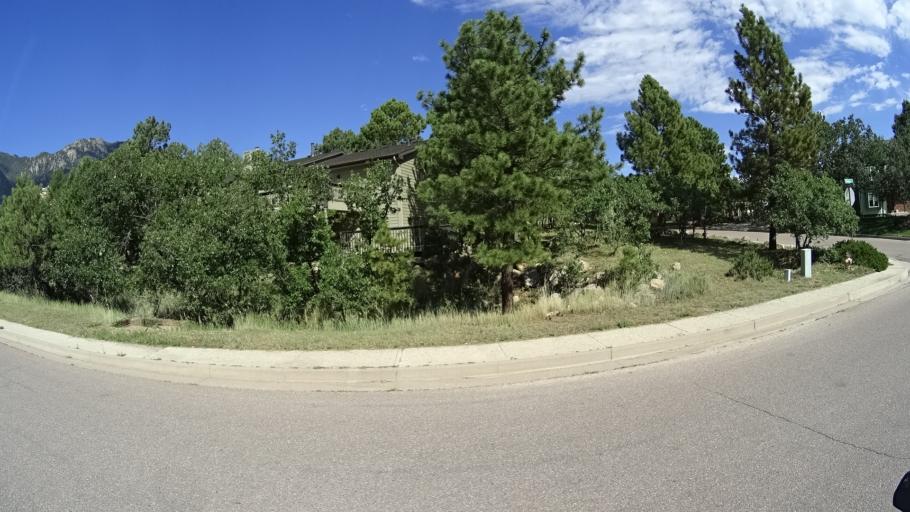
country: US
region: Colorado
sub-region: El Paso County
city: Fort Carson
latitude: 38.7635
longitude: -104.8288
